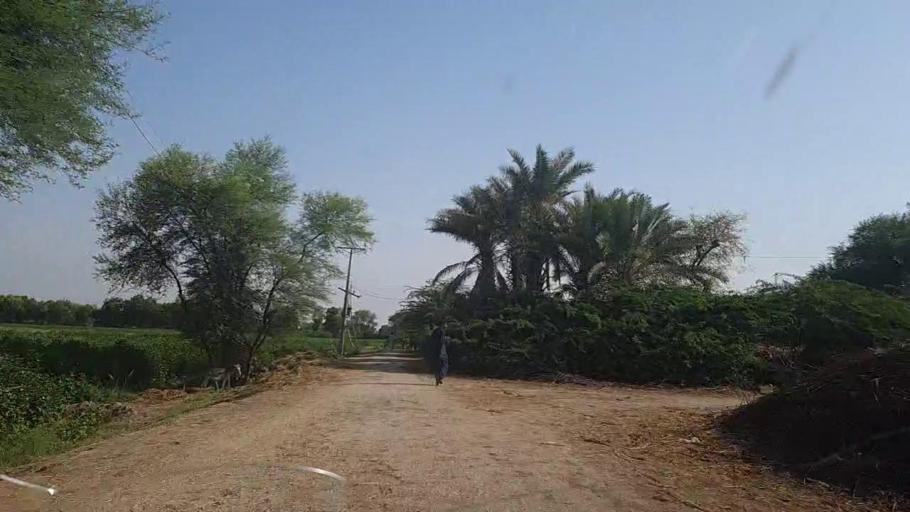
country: PK
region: Sindh
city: Khanpur
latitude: 27.7300
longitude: 69.3321
